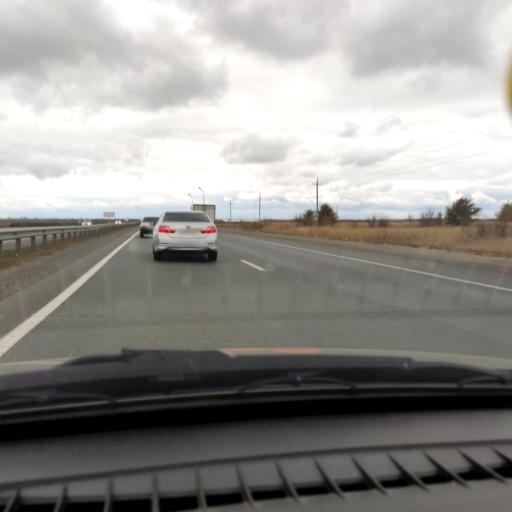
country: RU
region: Samara
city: Zhigulevsk
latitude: 53.5463
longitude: 49.5110
